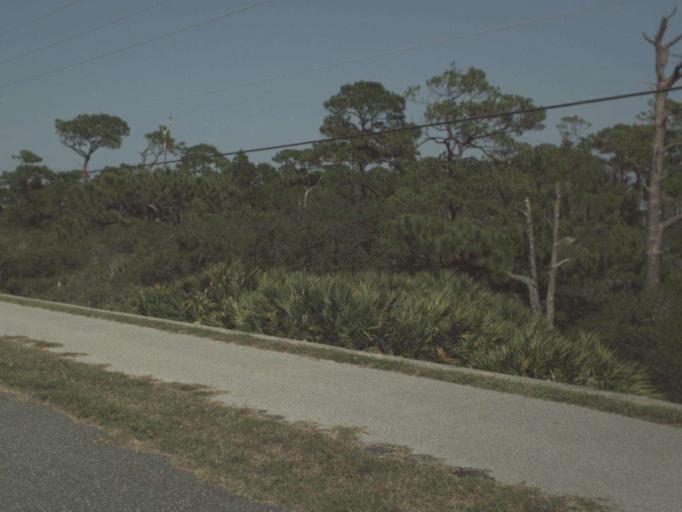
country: US
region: Florida
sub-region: Gulf County
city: Port Saint Joe
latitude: 29.7261
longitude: -85.3887
